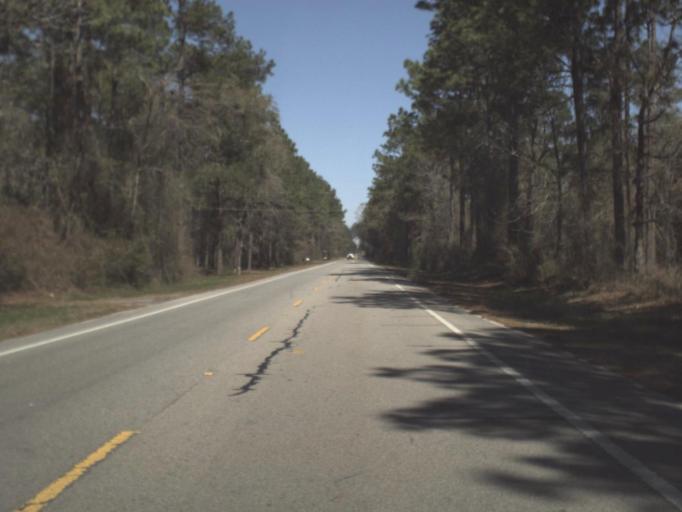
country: US
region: Florida
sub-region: Leon County
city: Woodville
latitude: 30.3098
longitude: -84.3118
